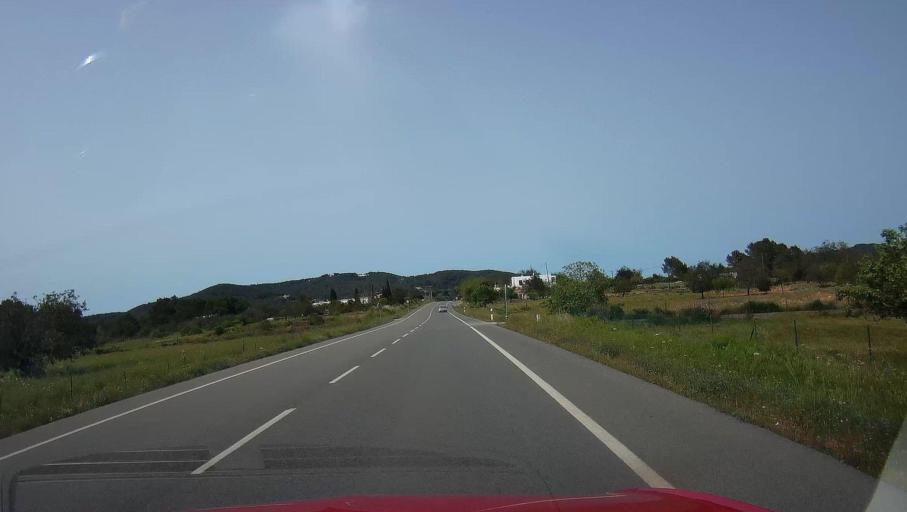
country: ES
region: Balearic Islands
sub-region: Illes Balears
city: Santa Eularia des Riu
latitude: 39.0188
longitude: 1.4874
